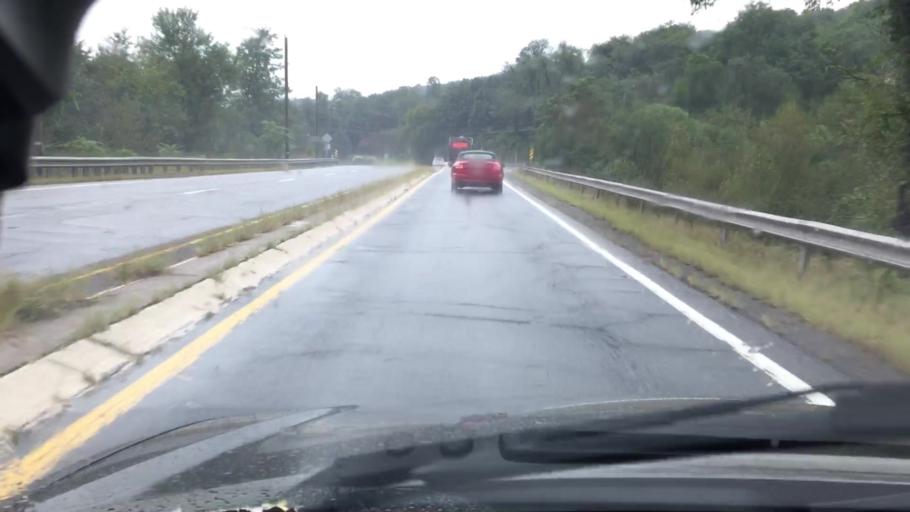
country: US
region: Pennsylvania
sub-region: Luzerne County
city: Nanticoke
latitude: 41.2173
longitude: -75.9946
